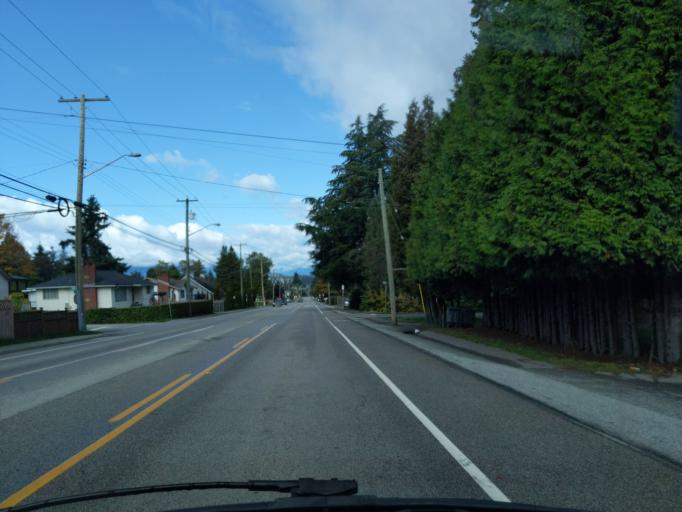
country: CA
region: British Columbia
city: New Westminster
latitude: 49.1958
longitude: -122.8564
